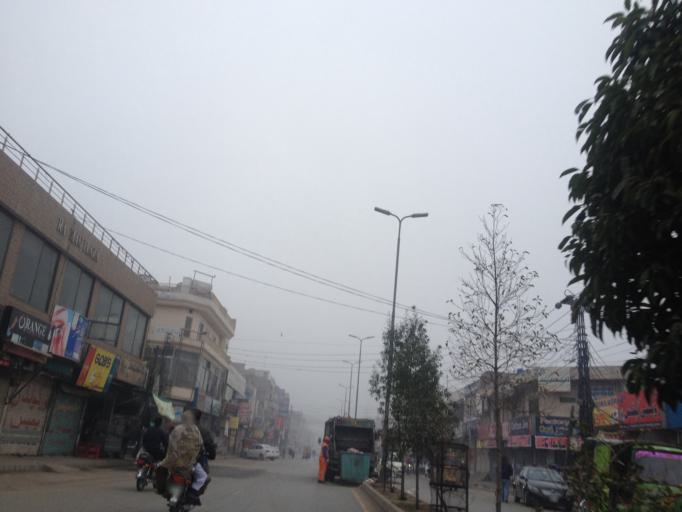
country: PK
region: Punjab
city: Lahore
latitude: 31.4582
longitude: 74.3025
